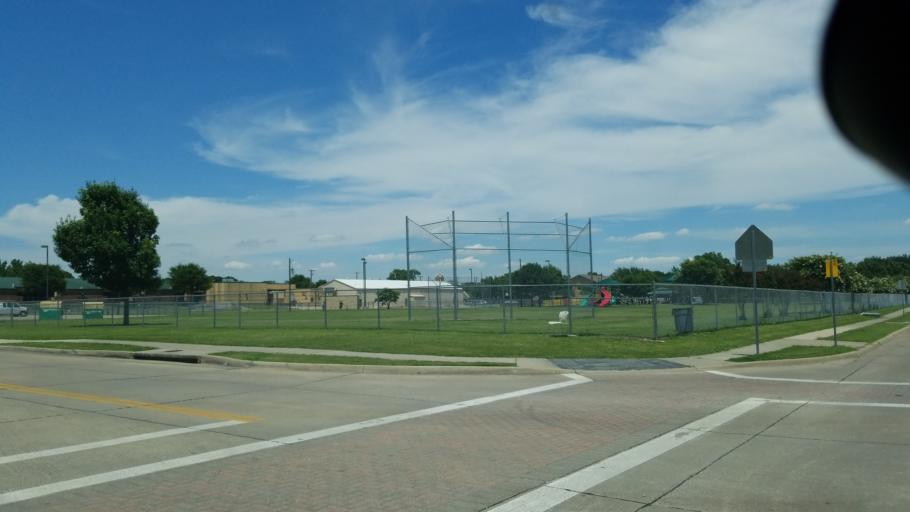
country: US
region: Texas
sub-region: Dallas County
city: Irving
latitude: 32.8289
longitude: -96.9699
